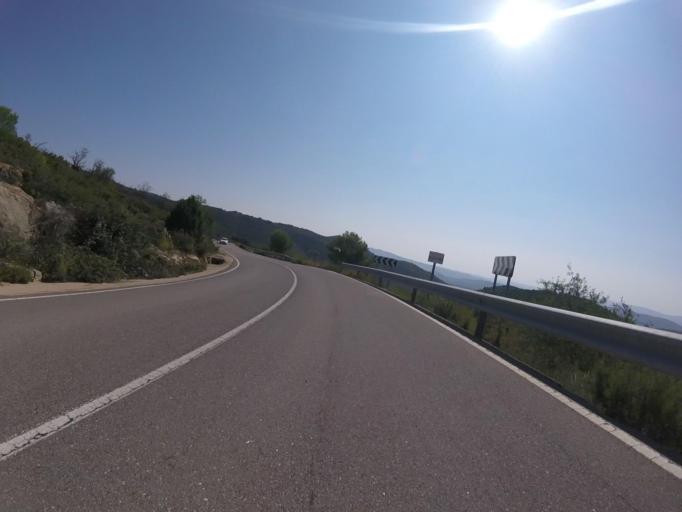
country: ES
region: Valencia
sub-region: Provincia de Castello
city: Benafigos
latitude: 40.2638
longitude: -0.2211
